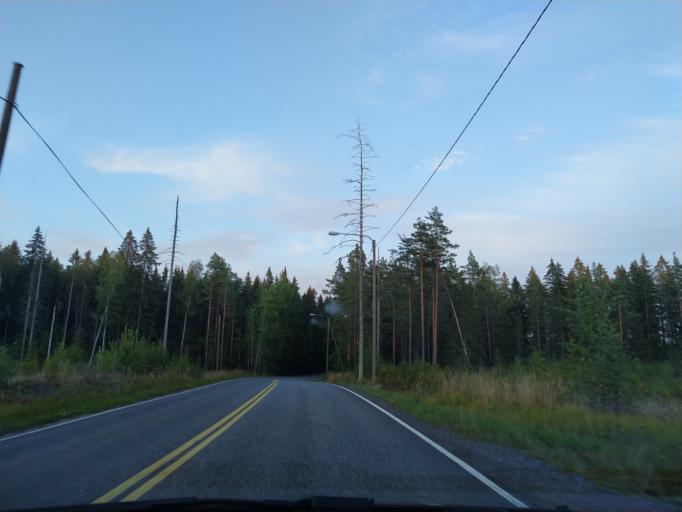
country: FI
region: Uusimaa
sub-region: Helsinki
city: Tuusula
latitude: 60.3534
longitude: 25.0294
